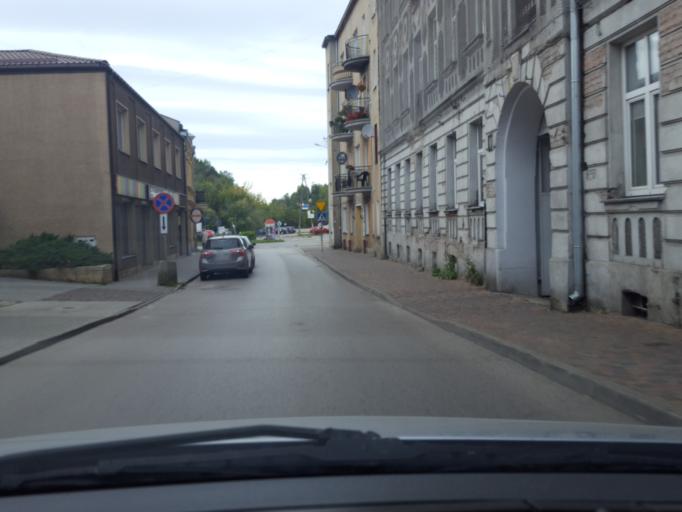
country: PL
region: Lodz Voivodeship
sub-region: Powiat brzezinski
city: Brzeziny
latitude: 51.8006
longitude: 19.7540
